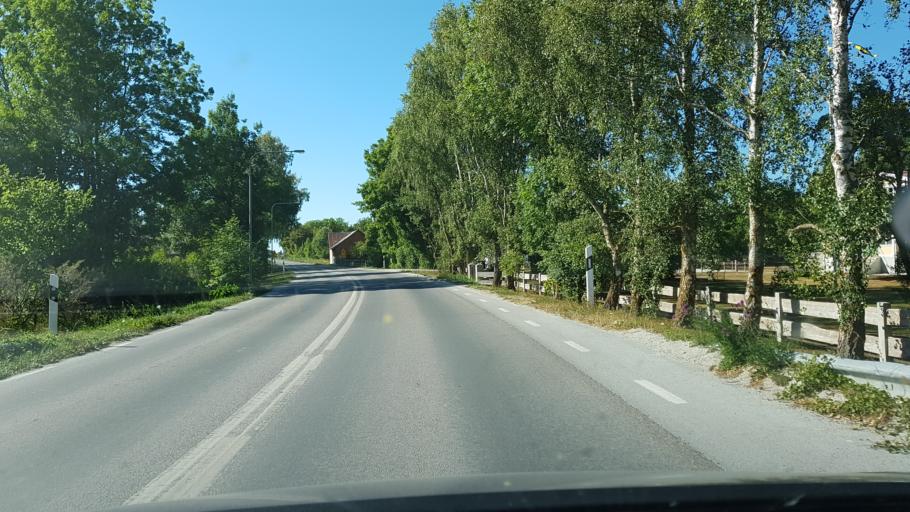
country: SE
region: Gotland
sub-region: Gotland
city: Klintehamn
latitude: 57.4456
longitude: 18.1447
